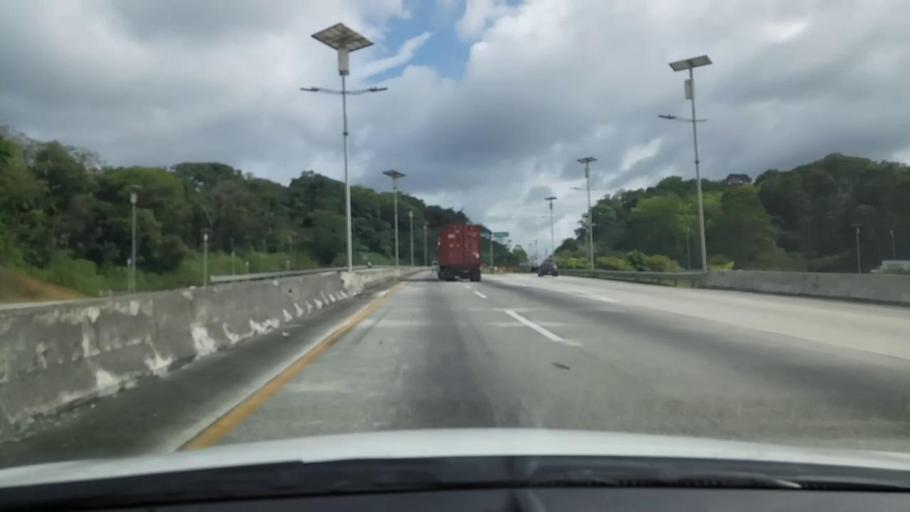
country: PA
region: Panama
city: Chilibre
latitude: 9.1245
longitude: -79.6191
